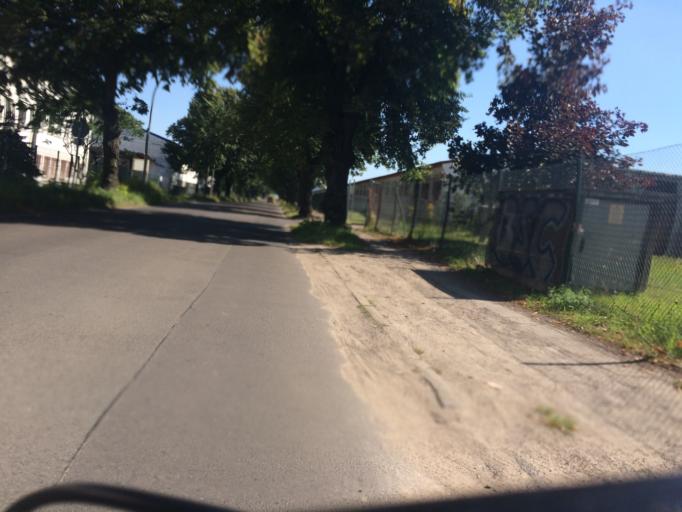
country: DE
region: Berlin
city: Buchholz
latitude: 52.5943
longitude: 13.4274
